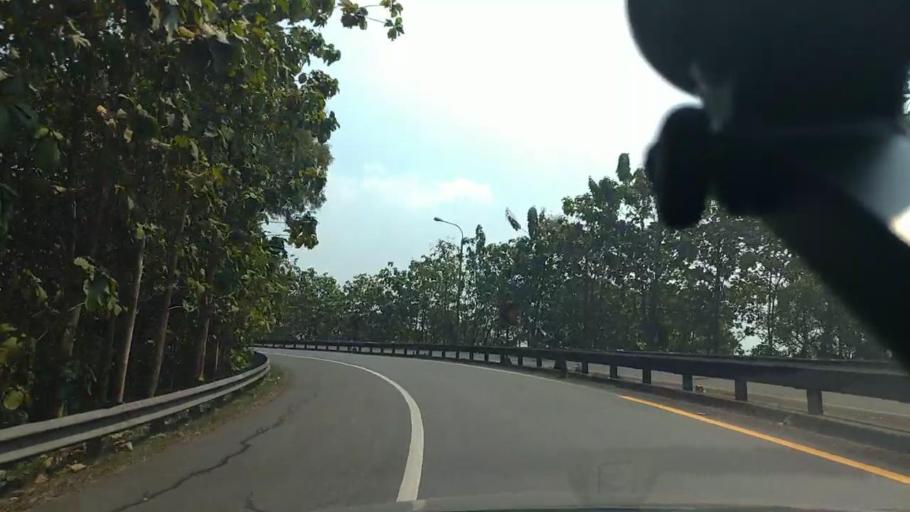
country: ID
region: Banten
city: Serang
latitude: -6.1139
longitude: 106.1861
